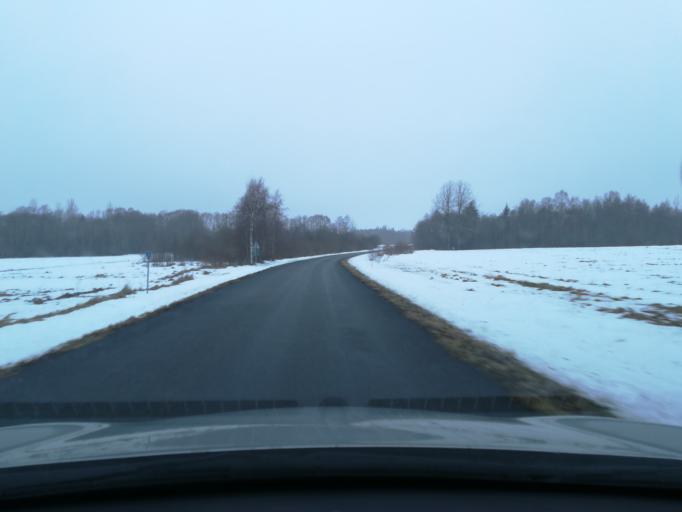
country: EE
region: Harju
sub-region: Raasiku vald
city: Raasiku
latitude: 59.3386
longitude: 25.2339
